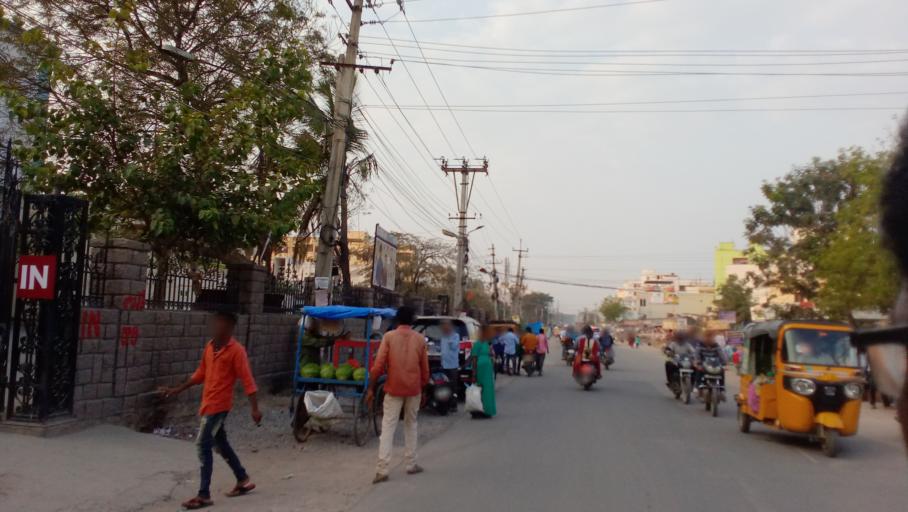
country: IN
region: Telangana
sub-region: Medak
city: Serilingampalle
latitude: 17.4981
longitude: 78.3175
